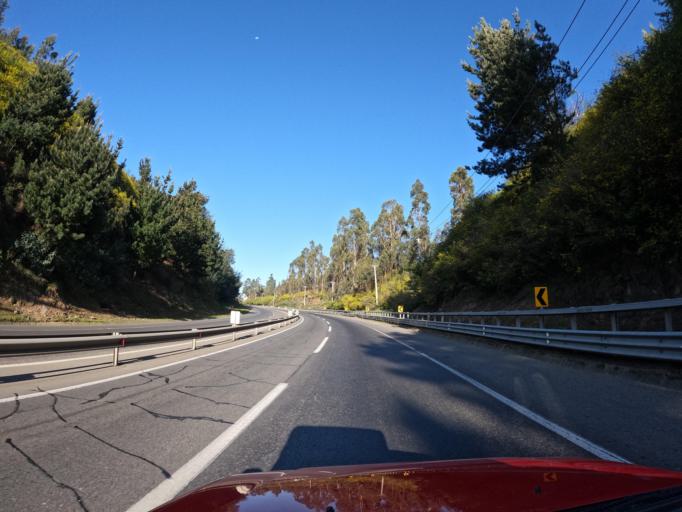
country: CL
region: Biobio
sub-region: Provincia de Concepcion
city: Penco
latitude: -36.7605
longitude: -72.9747
